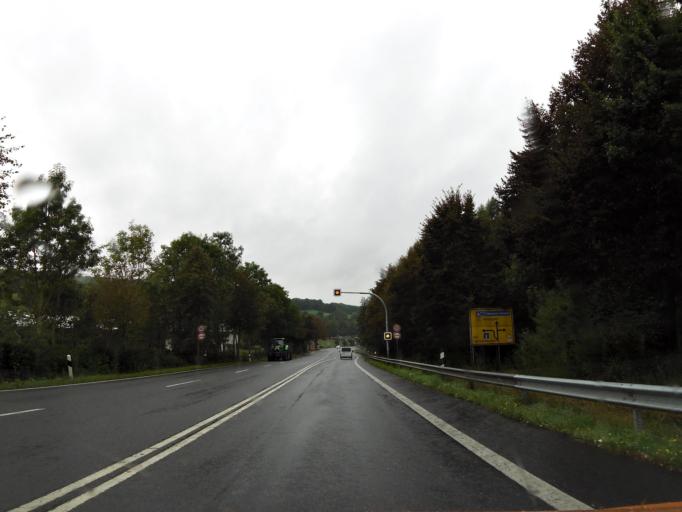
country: DE
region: Lower Saxony
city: Goettingen
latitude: 51.5482
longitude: 9.9811
